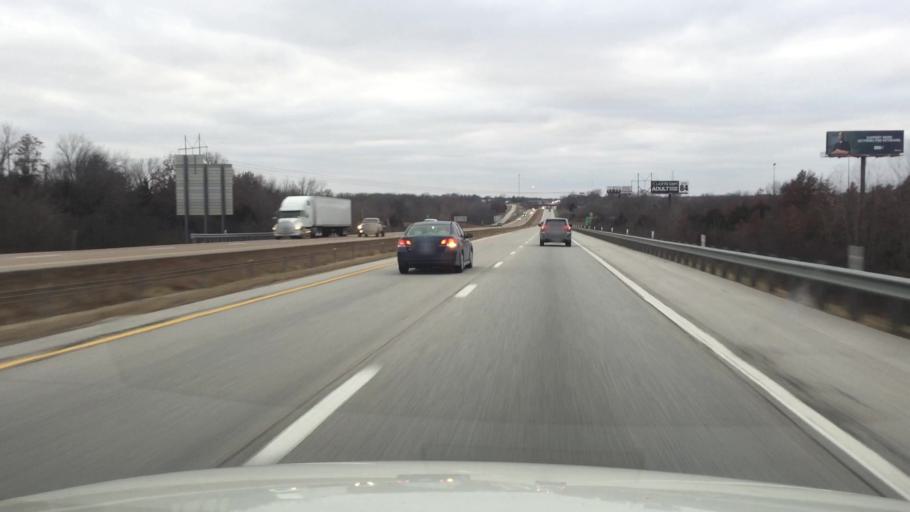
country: US
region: Missouri
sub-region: Cooper County
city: Boonville
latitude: 38.9358
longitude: -92.7833
